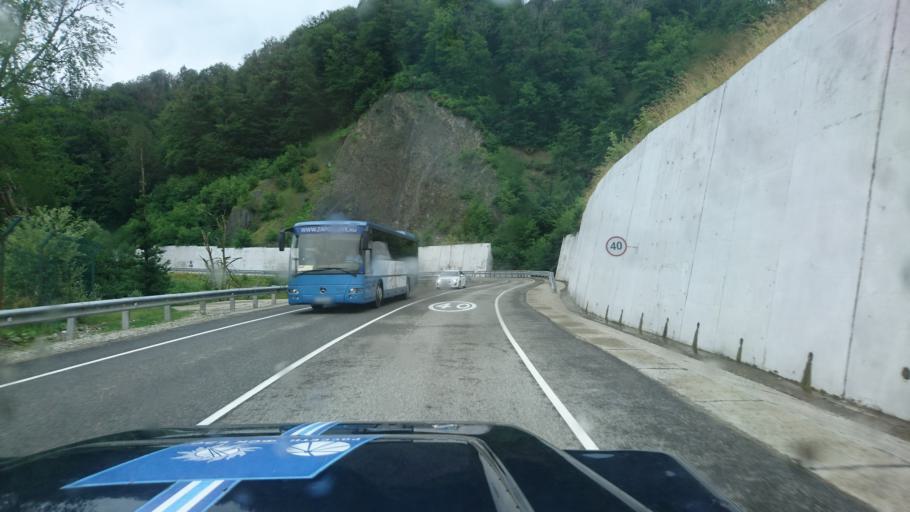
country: RU
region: Krasnodarskiy
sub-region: Sochi City
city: Krasnaya Polyana
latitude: 43.6670
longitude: 40.2925
